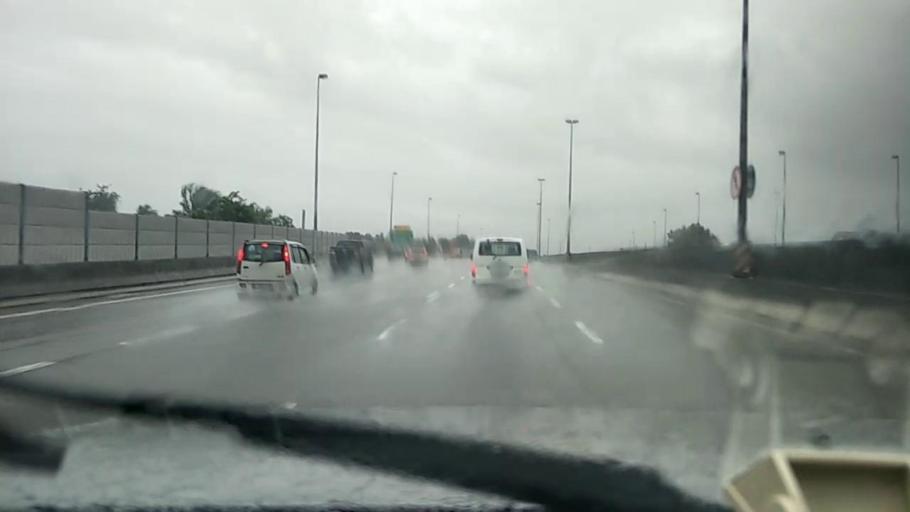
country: MY
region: Selangor
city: Kampong Baharu Balakong
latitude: 2.9907
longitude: 101.7700
